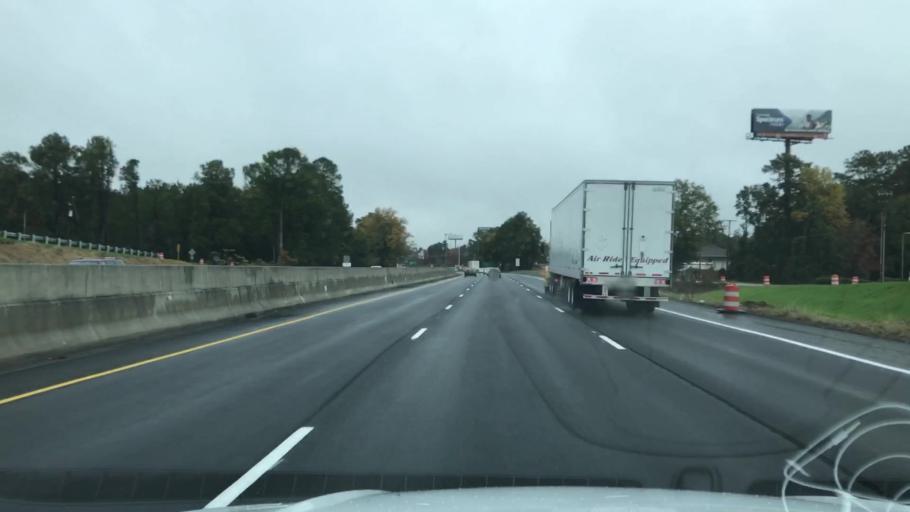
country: US
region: South Carolina
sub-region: Lexington County
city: Springdale
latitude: 33.9895
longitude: -81.1072
